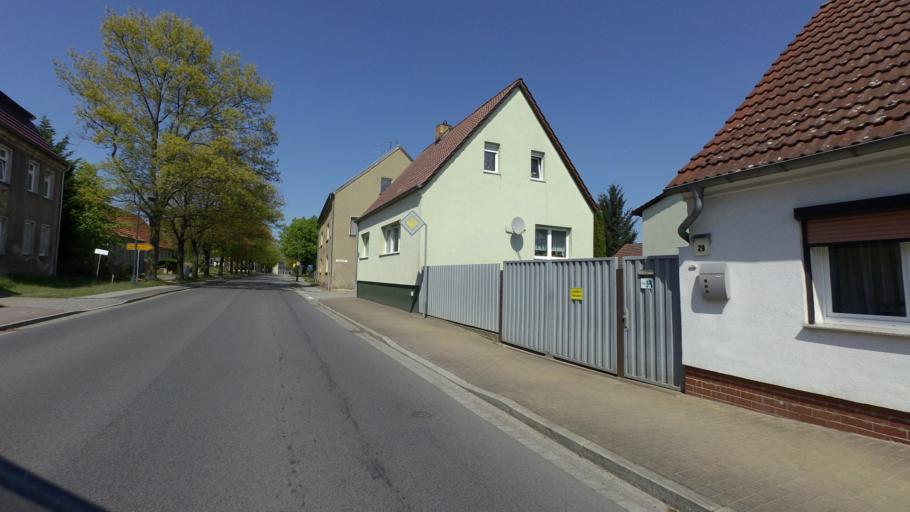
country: DE
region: Brandenburg
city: Lieberose
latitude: 51.9831
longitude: 14.2997
